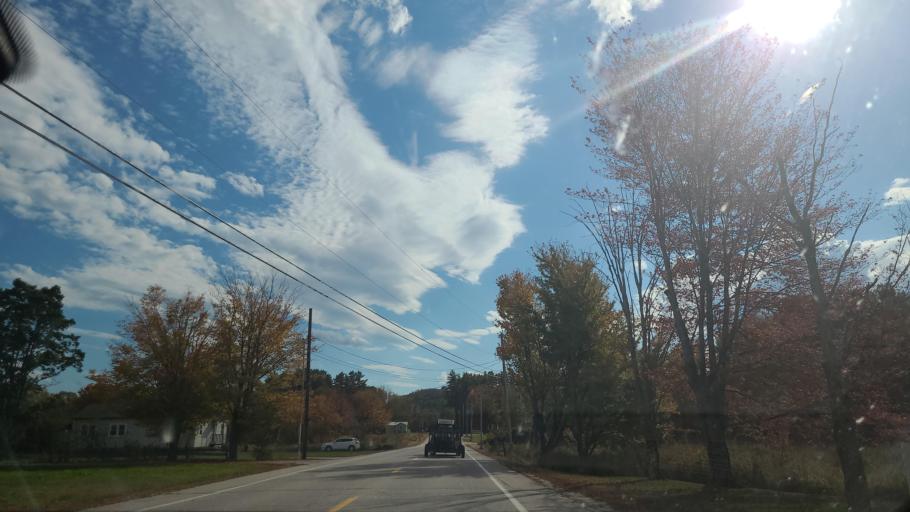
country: US
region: New Hampshire
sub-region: Carroll County
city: Conway
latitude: 44.0142
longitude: -71.1312
